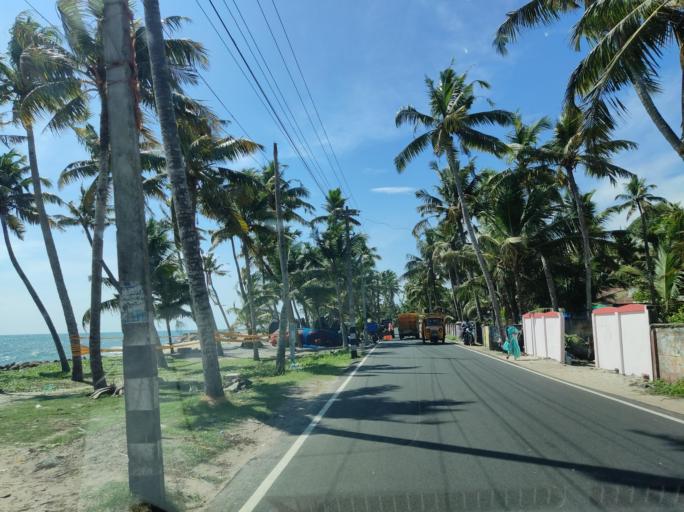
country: IN
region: Kerala
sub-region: Alappuzha
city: Kayankulam
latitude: 9.2554
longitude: 76.4086
